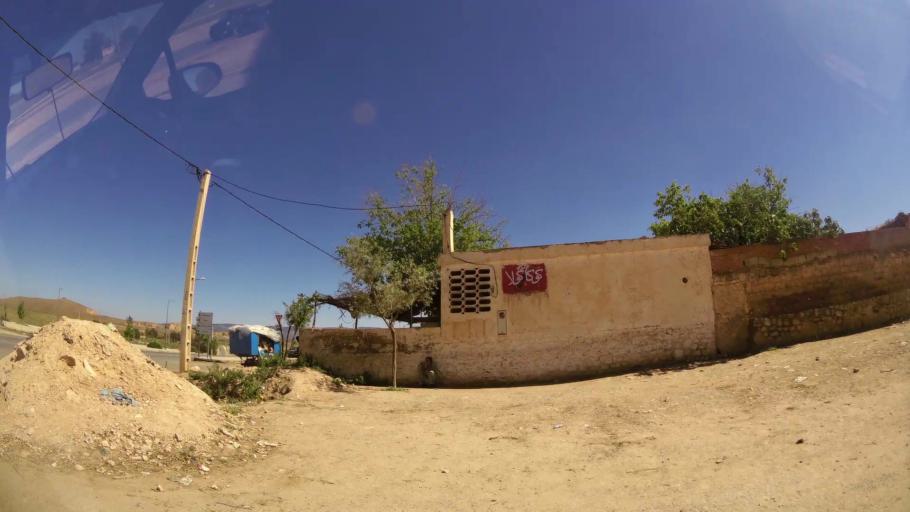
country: MA
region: Oriental
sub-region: Oujda-Angad
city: Oujda
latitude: 34.6627
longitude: -1.8670
